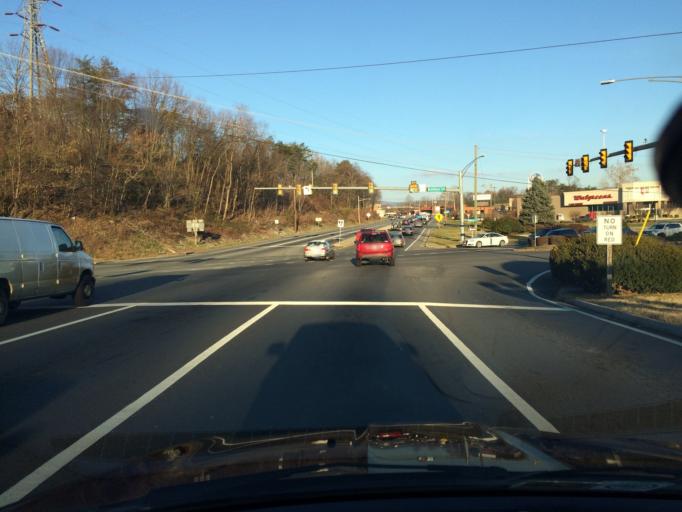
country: US
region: Virginia
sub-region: Roanoke County
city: Cave Spring
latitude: 37.2298
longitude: -80.0081
